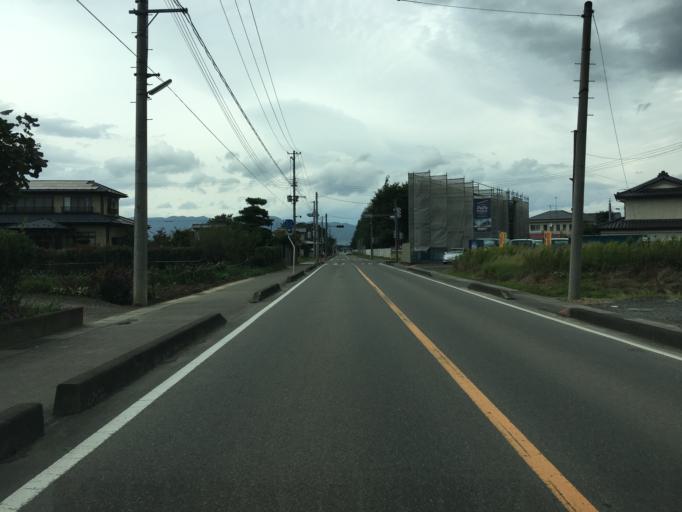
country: JP
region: Fukushima
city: Hobaramachi
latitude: 37.8295
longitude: 140.5571
